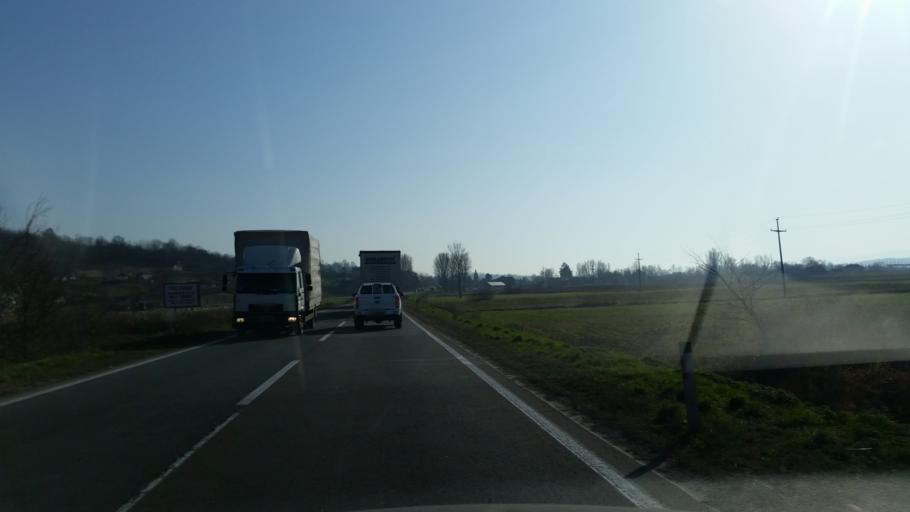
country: RS
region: Central Serbia
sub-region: Kolubarski Okrug
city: Lajkovac
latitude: 44.3411
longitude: 20.2061
